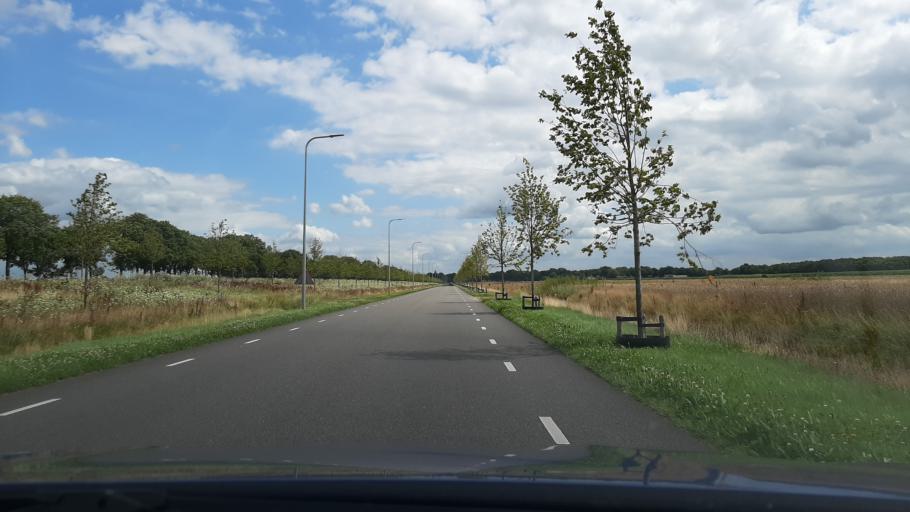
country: NL
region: Drenthe
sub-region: Gemeente Hoogeveen
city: Hoogeveen
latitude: 52.7009
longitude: 6.5174
